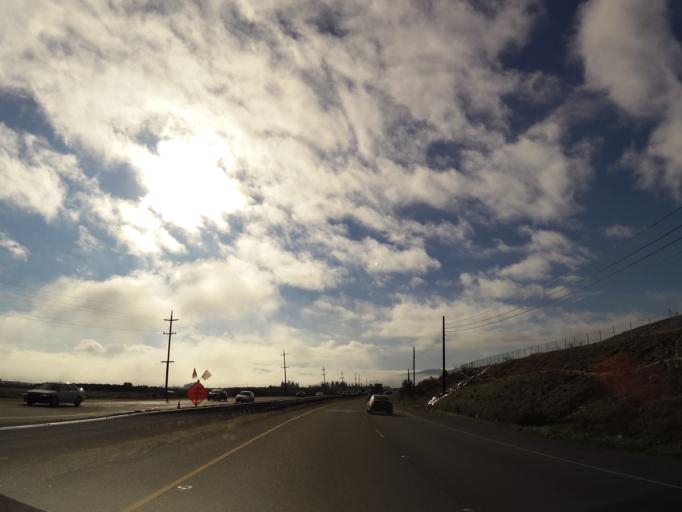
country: US
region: California
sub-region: Marin County
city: Novato
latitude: 38.1451
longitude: -122.5648
